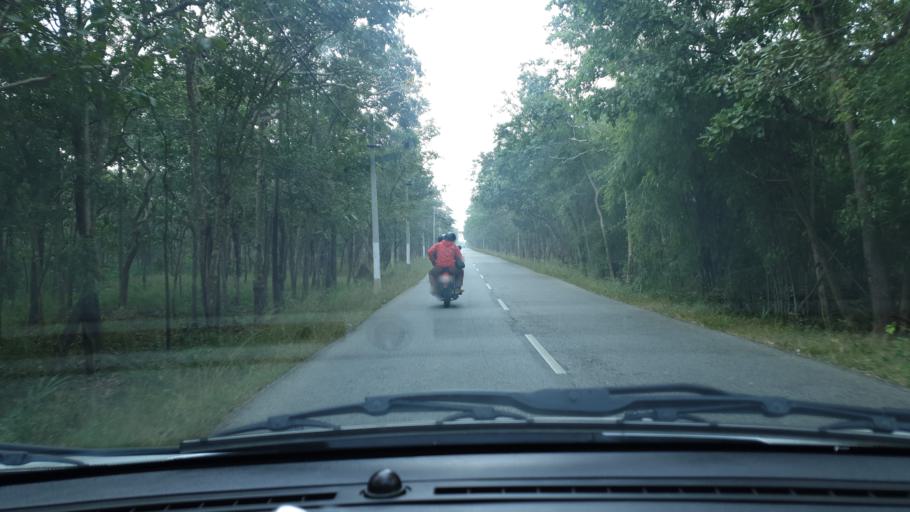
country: IN
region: Andhra Pradesh
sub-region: Kurnool
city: Srisailam
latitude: 16.2971
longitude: 78.7311
